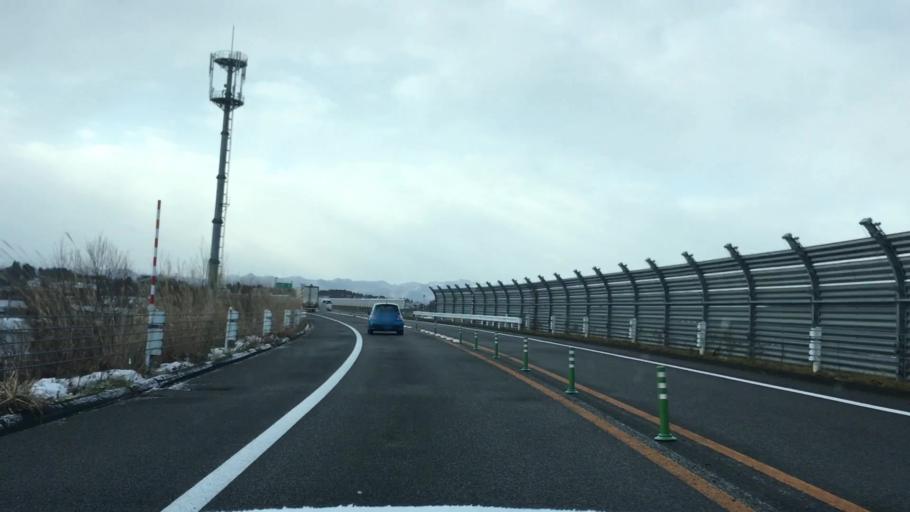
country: JP
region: Akita
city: Odate
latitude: 40.2871
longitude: 140.5416
